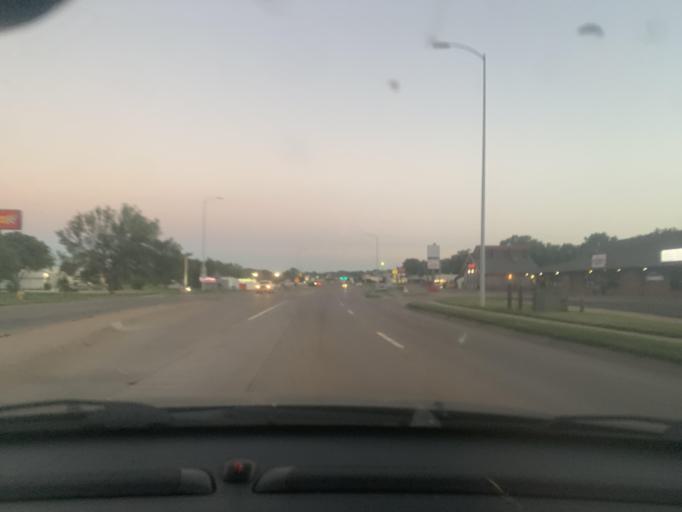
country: US
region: Nebraska
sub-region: Douglas County
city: Ralston
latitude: 41.2949
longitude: -96.0527
